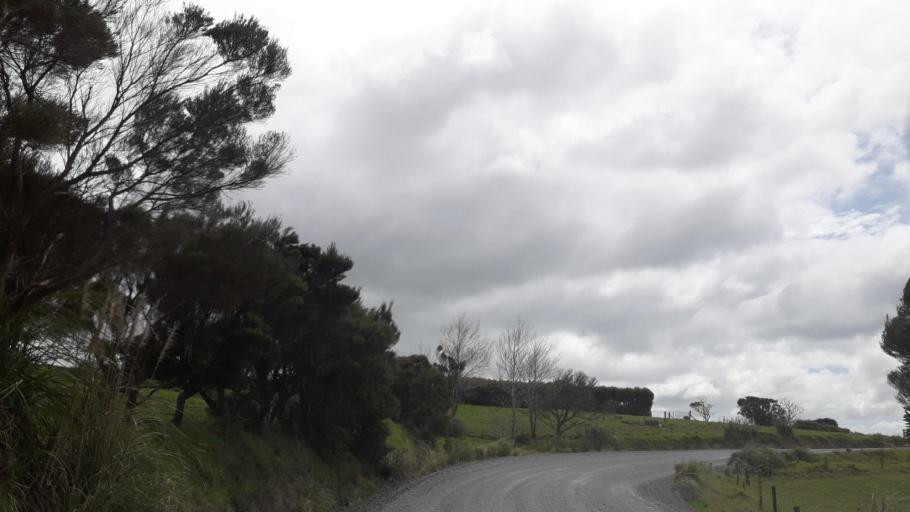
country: NZ
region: Northland
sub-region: Far North District
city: Taipa
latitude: -35.0024
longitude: 173.4311
